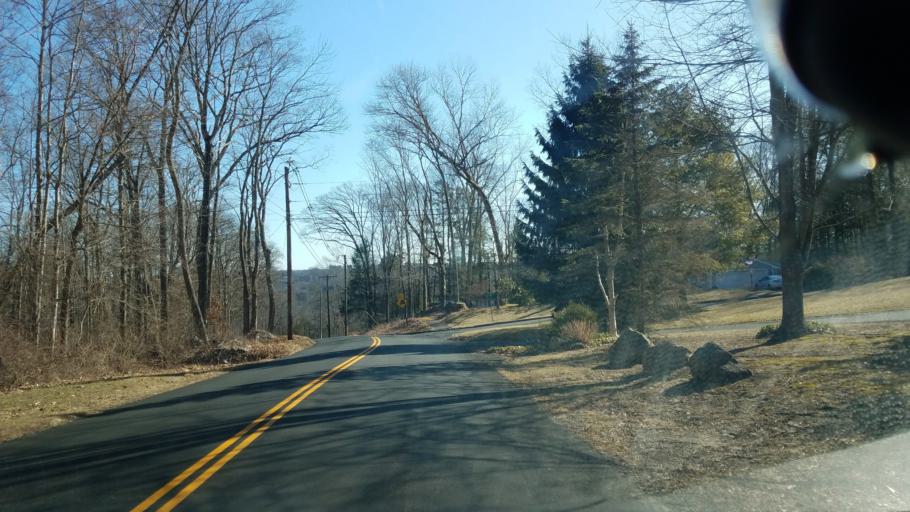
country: US
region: Connecticut
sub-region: Litchfield County
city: New Milford
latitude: 41.4872
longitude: -73.4249
